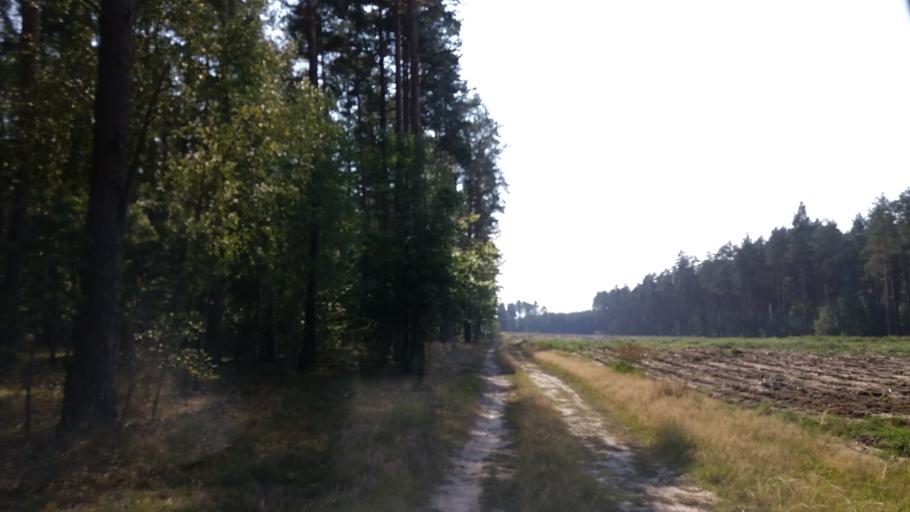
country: PL
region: West Pomeranian Voivodeship
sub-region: Powiat drawski
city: Kalisz Pomorski
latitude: 53.1284
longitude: 15.9452
